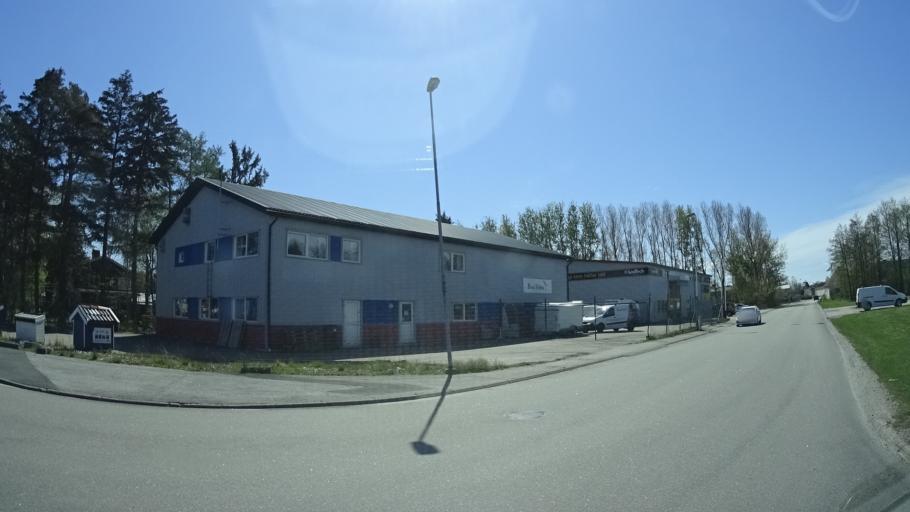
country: SE
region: Vaestra Goetaland
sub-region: Stenungsunds Kommun
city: Stenungsund
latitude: 58.0781
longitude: 11.8249
